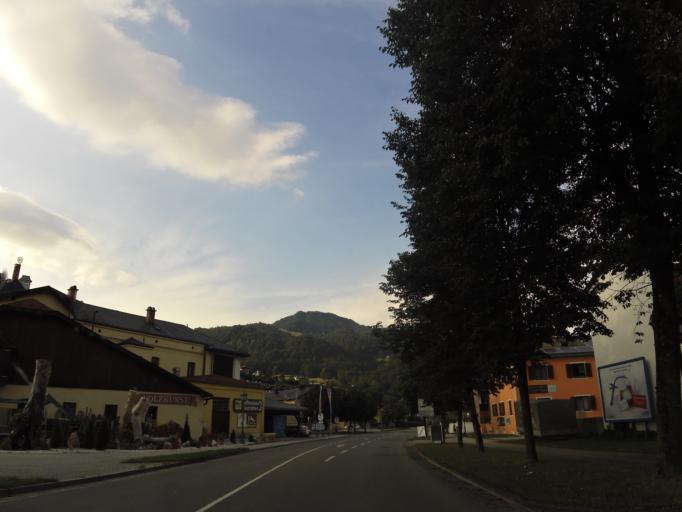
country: DE
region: Bavaria
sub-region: Upper Bavaria
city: Berchtesgaden
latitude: 47.6337
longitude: 13.0075
